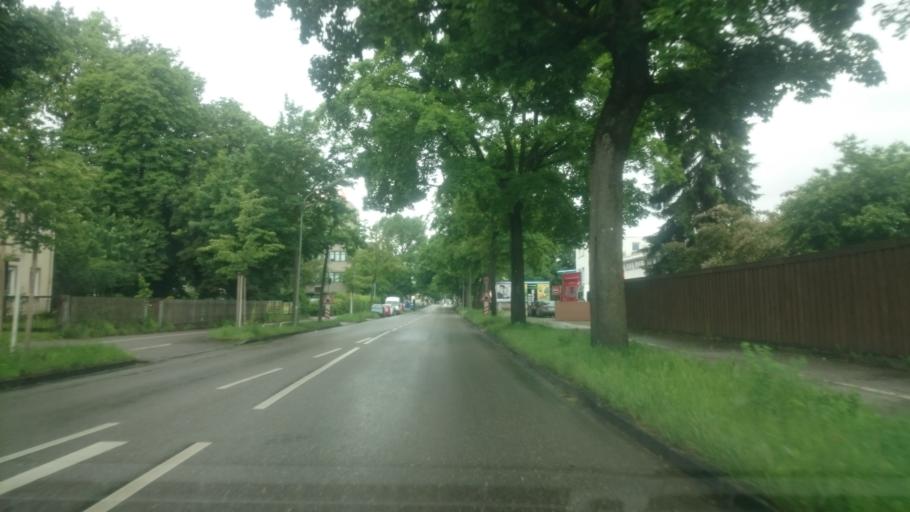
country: DE
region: Bavaria
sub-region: Swabia
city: Augsburg
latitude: 48.3712
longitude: 10.9375
